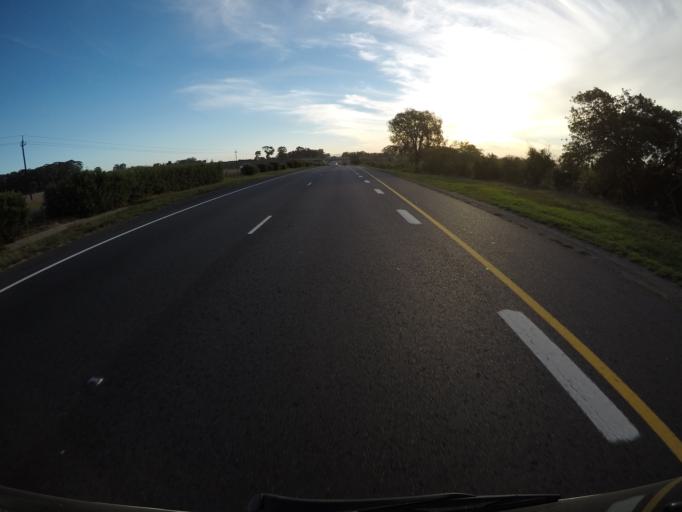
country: ZA
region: Western Cape
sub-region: City of Cape Town
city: Kraaifontein
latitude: -33.8184
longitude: 18.7964
